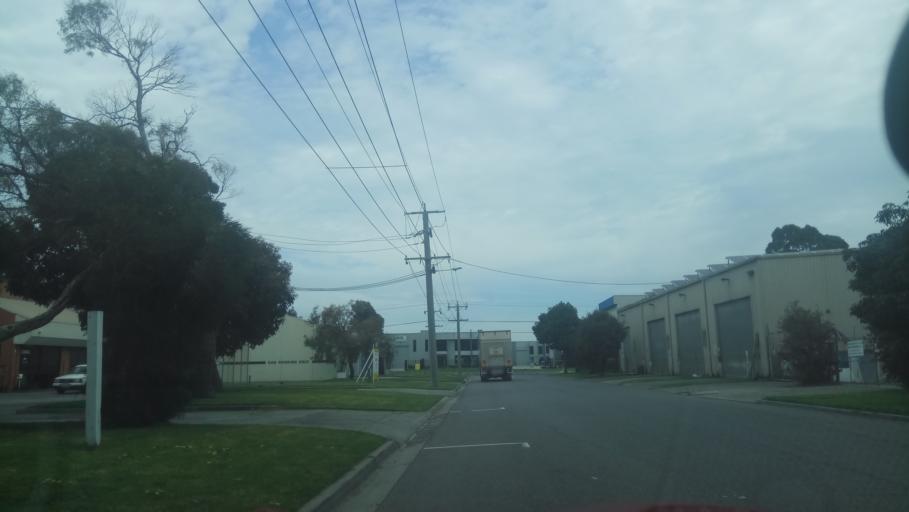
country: AU
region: Victoria
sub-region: Kingston
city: Aspendale Gardens
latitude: -38.0070
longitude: 145.1107
